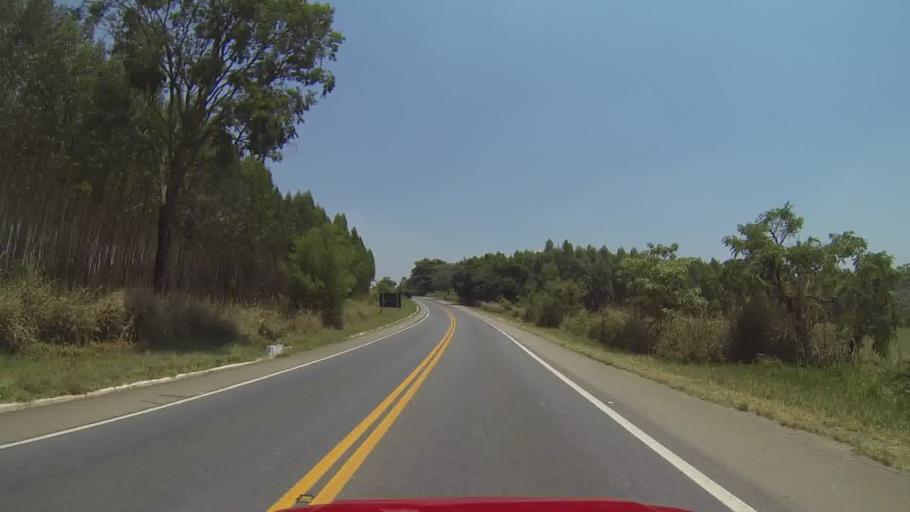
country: BR
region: Minas Gerais
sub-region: Itapecerica
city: Itapecerica
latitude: -20.3073
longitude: -45.2125
